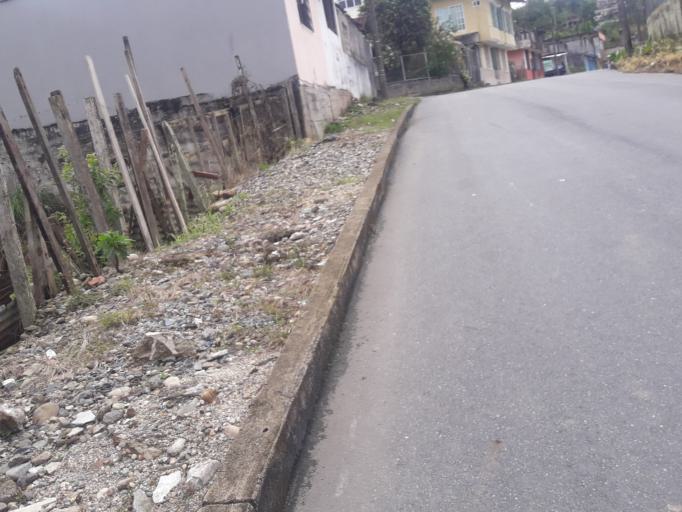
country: EC
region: Napo
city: Tena
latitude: -0.9978
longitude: -77.8107
